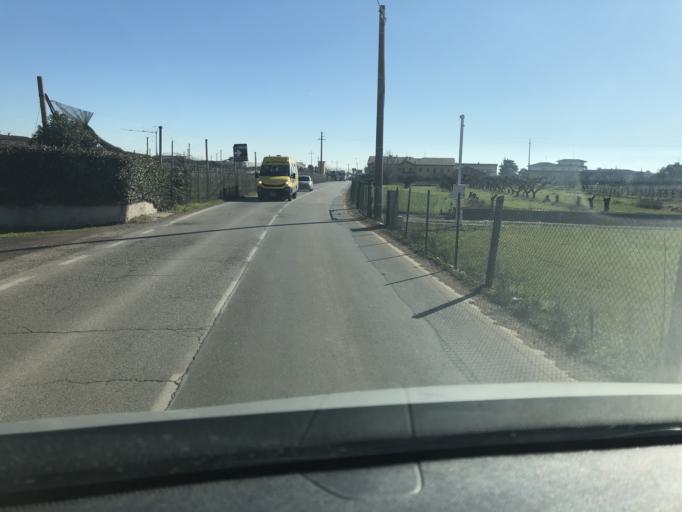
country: IT
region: Veneto
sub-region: Provincia di Verona
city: Lugagnano
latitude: 45.4350
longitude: 10.8688
